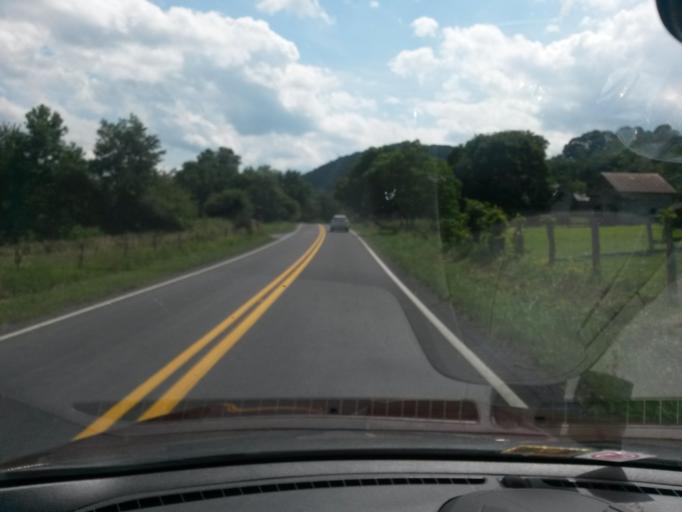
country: US
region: West Virginia
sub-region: Pendleton County
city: Franklin
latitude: 38.5516
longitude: -79.4422
